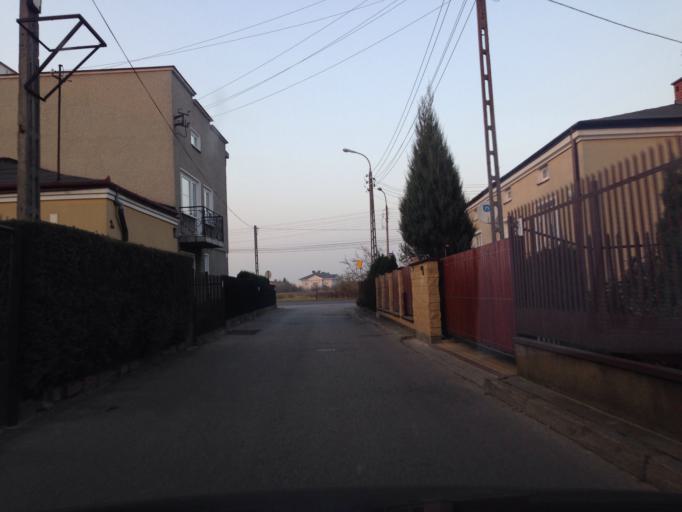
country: PL
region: Masovian Voivodeship
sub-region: Powiat pruszkowski
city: Rybie
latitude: 52.1587
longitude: 20.9410
